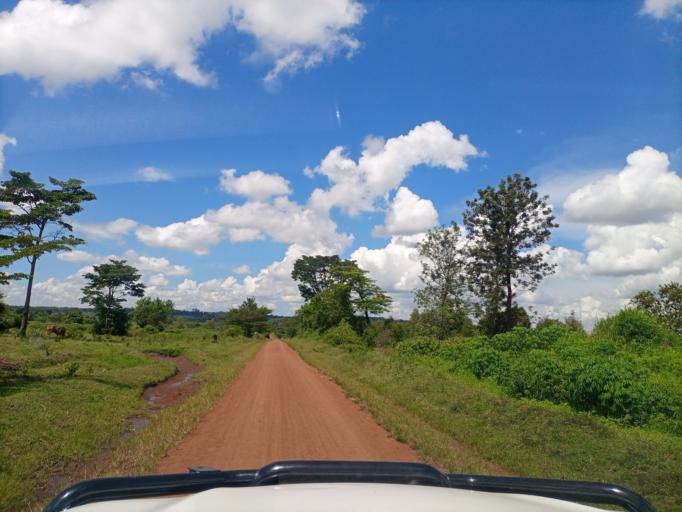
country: UG
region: Eastern Region
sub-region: Tororo District
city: Tororo
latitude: 0.7200
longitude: 34.0159
